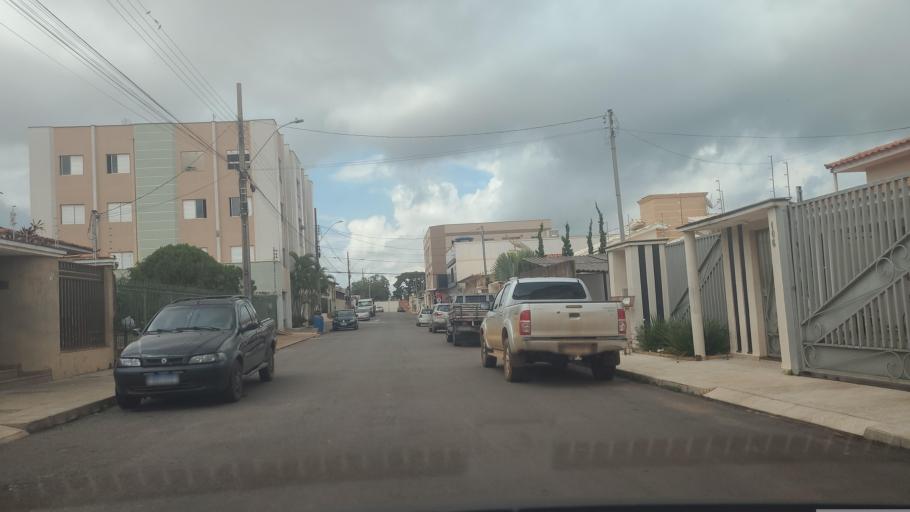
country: BR
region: Minas Gerais
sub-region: Carmo Do Paranaiba
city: Carmo do Paranaiba
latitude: -19.1965
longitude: -46.2391
